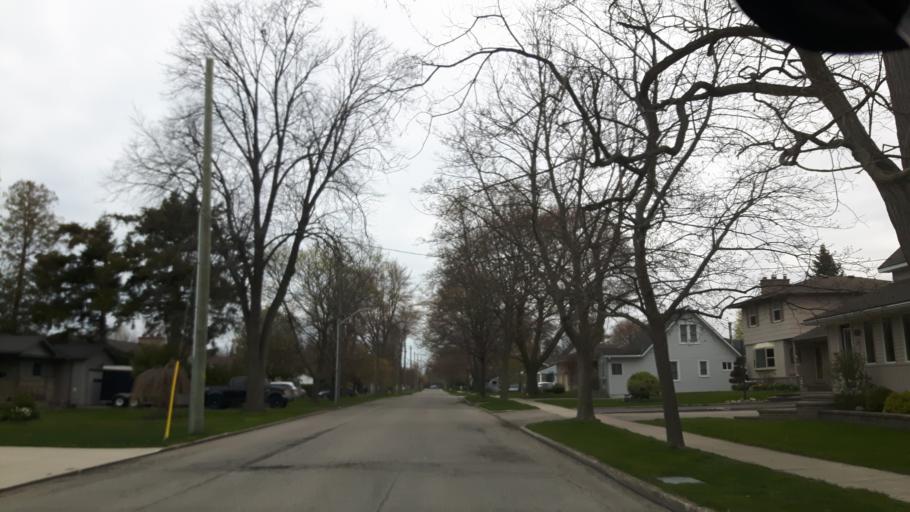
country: CA
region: Ontario
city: Goderich
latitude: 43.7355
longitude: -81.7215
